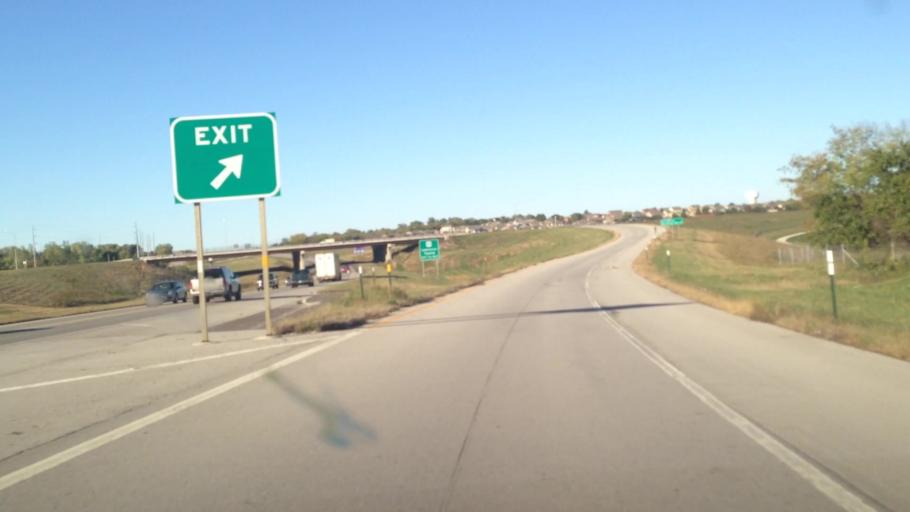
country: US
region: Kansas
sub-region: Douglas County
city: Lawrence
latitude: 38.9566
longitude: -95.3346
